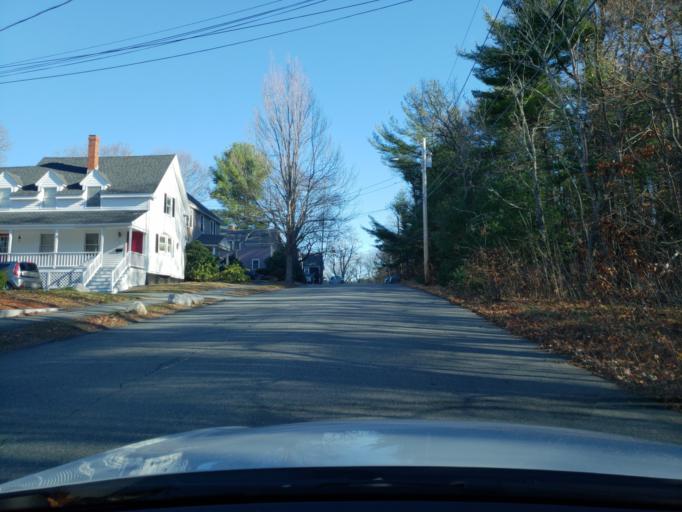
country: US
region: Massachusetts
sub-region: Essex County
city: Andover
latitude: 42.6536
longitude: -71.1313
